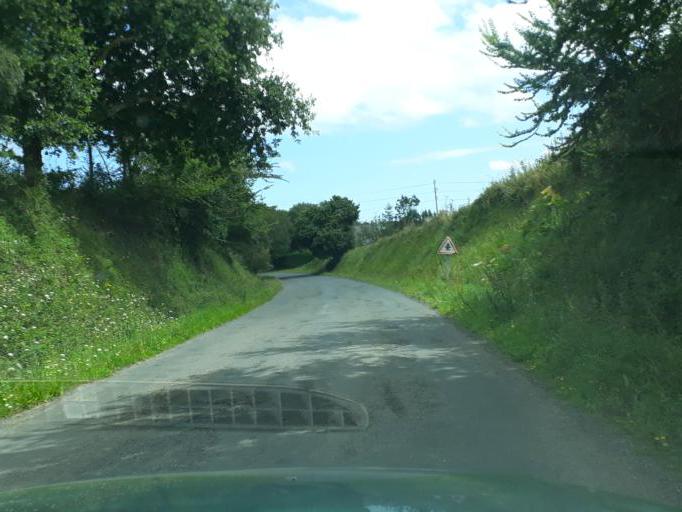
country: FR
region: Brittany
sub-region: Departement des Cotes-d'Armor
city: Paimpol
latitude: 48.7724
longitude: -3.0696
